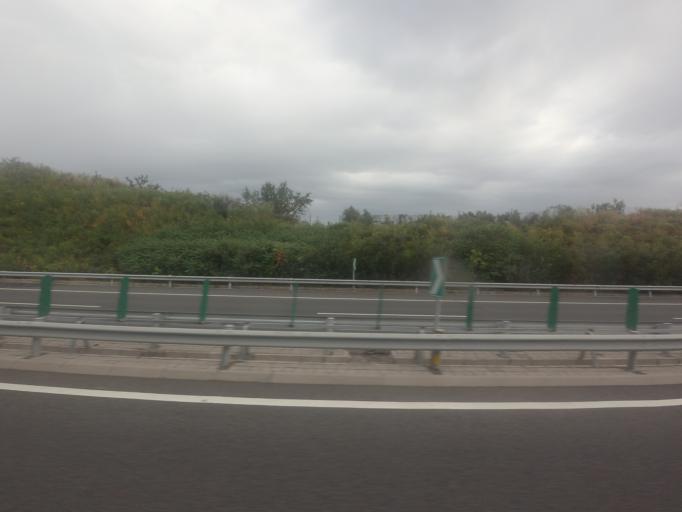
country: CN
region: Beijing
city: Dachengzi
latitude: 40.4062
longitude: 117.1235
